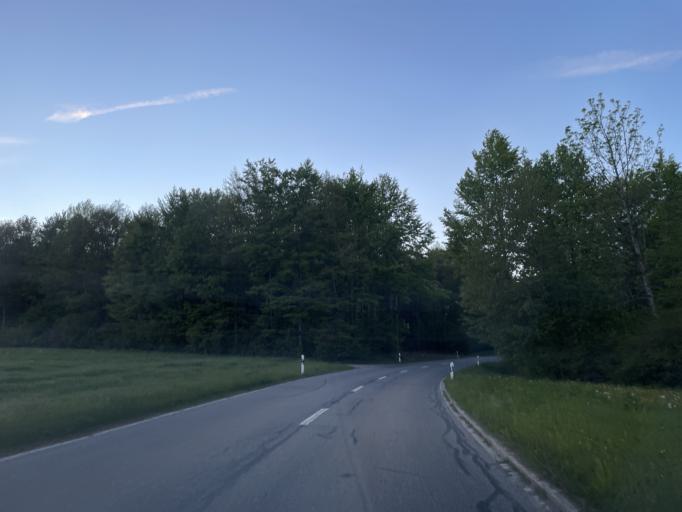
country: CH
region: Zurich
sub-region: Bezirk Winterthur
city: Brutten
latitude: 47.4631
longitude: 8.6796
